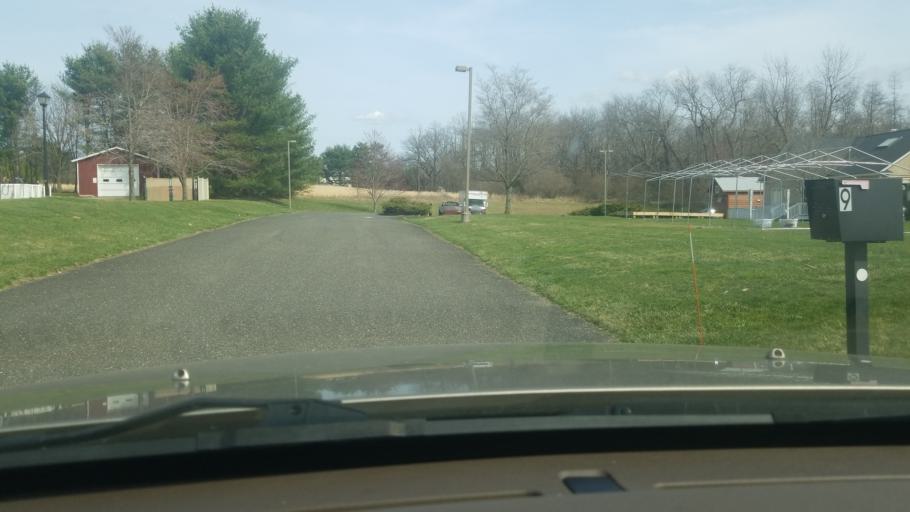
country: US
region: New Jersey
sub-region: Monmouth County
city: West Freehold
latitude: 40.2521
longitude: -74.3415
